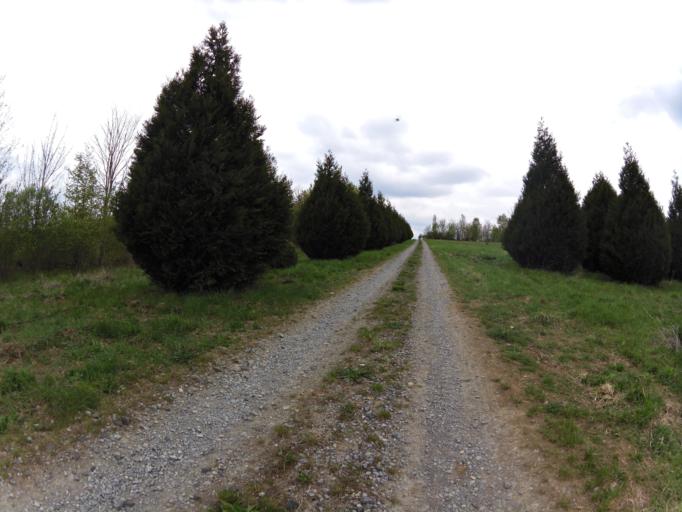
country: DE
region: Bavaria
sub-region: Regierungsbezirk Unterfranken
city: Greussenheim
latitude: 49.8185
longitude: 9.7874
